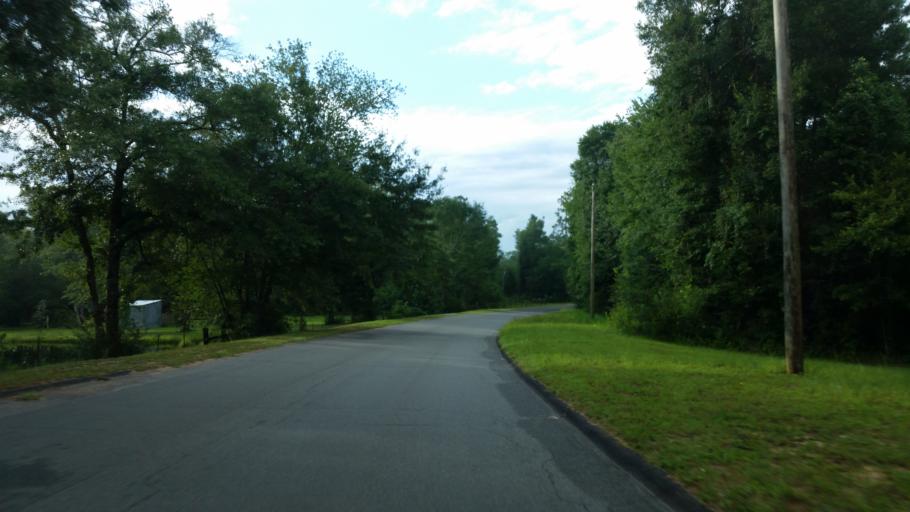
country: US
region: Florida
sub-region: Okaloosa County
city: Crestview
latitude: 30.6808
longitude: -86.7494
